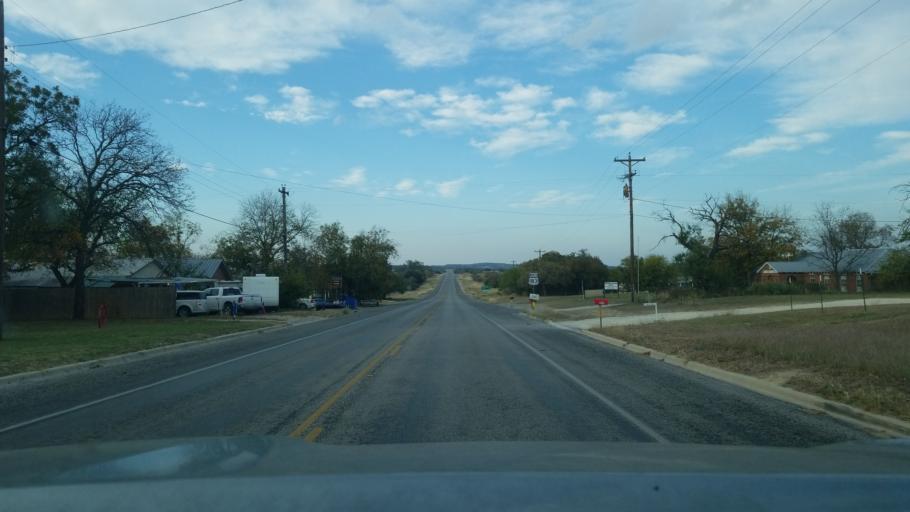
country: US
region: Texas
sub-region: Brown County
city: Lake Brownwood
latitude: 31.9817
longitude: -98.9206
